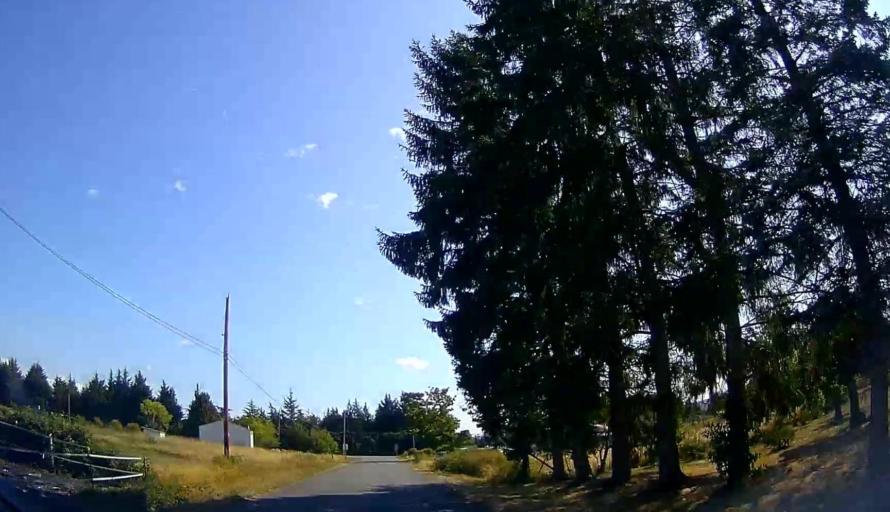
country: US
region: Washington
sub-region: Skagit County
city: Burlington
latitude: 48.4884
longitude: -122.4639
